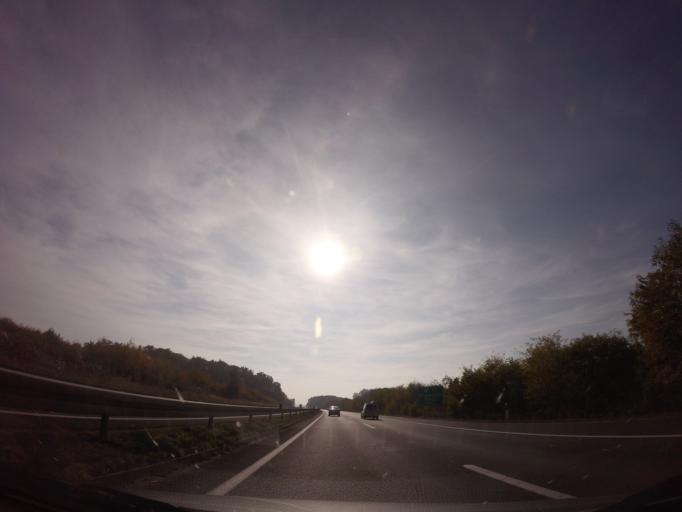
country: HR
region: Grad Zagreb
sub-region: Sesvete
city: Sesvete
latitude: 45.8400
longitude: 16.1398
